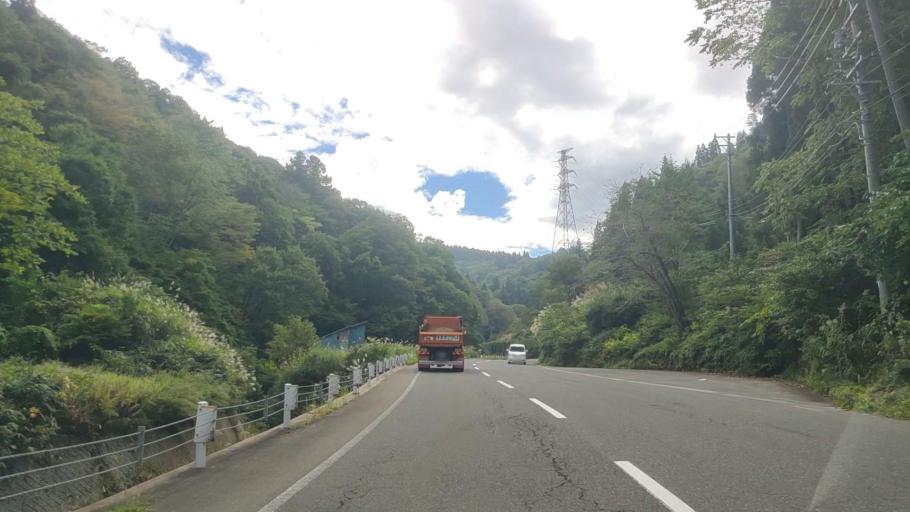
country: JP
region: Nagano
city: Iiyama
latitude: 36.8932
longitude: 138.3221
